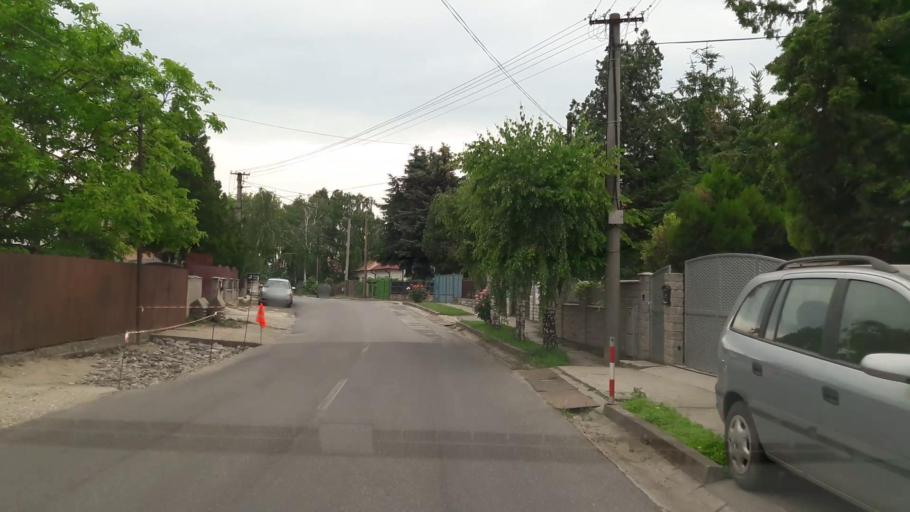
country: SK
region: Bratislavsky
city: Senec
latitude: 48.2170
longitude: 17.3616
